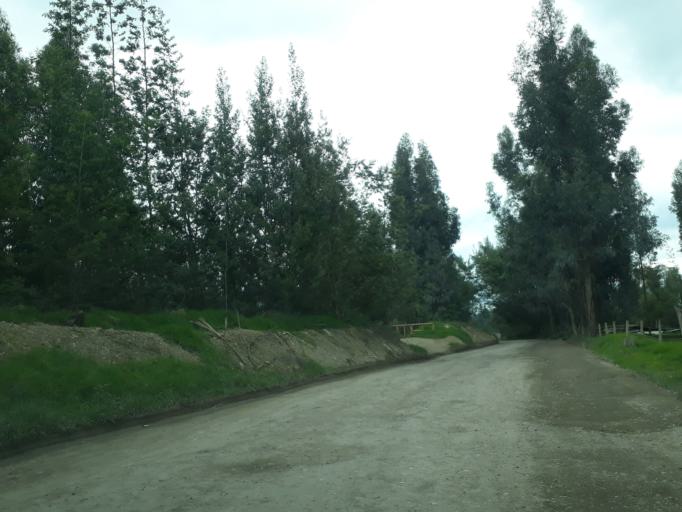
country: CO
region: Cundinamarca
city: Lenguazaque
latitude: 5.3236
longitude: -73.7570
